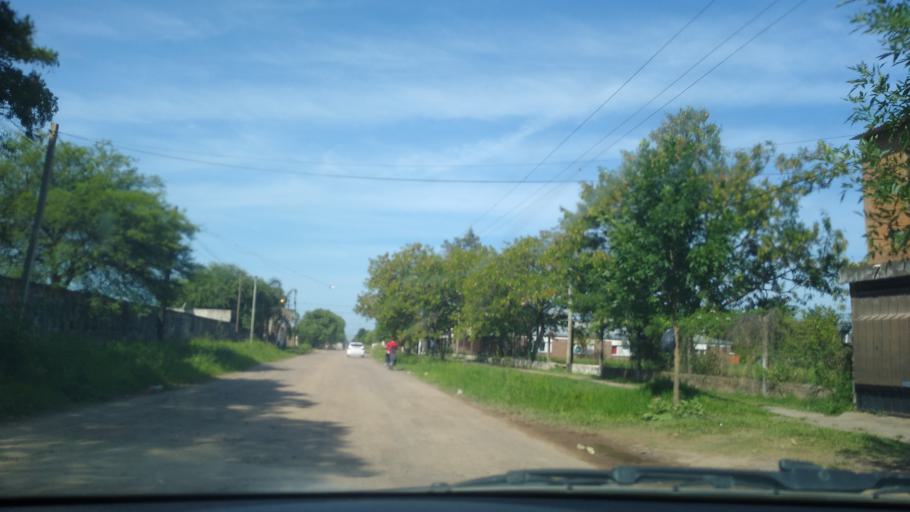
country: AR
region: Chaco
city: Barranqueras
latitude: -27.4950
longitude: -58.9549
